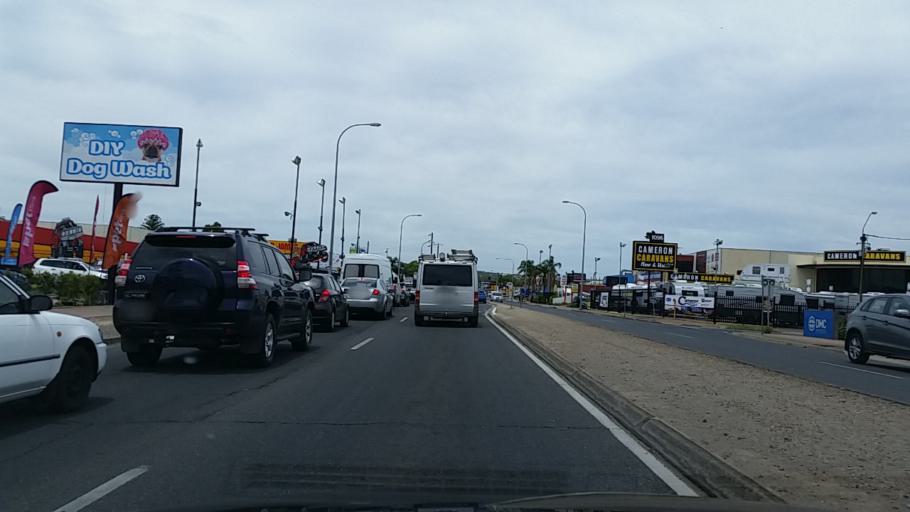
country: AU
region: South Australia
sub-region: Marion
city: Clovelly Park
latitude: -34.9906
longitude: 138.5747
